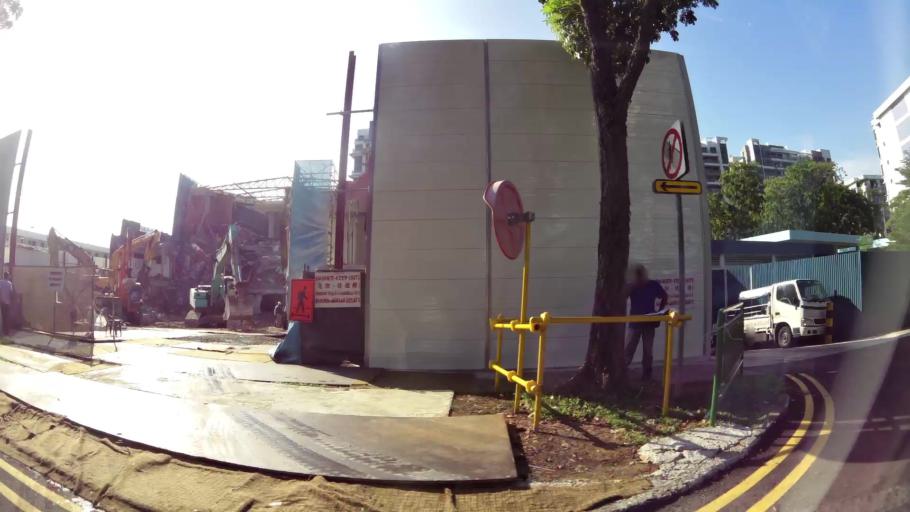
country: SG
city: Singapore
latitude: 1.3264
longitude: 103.9292
